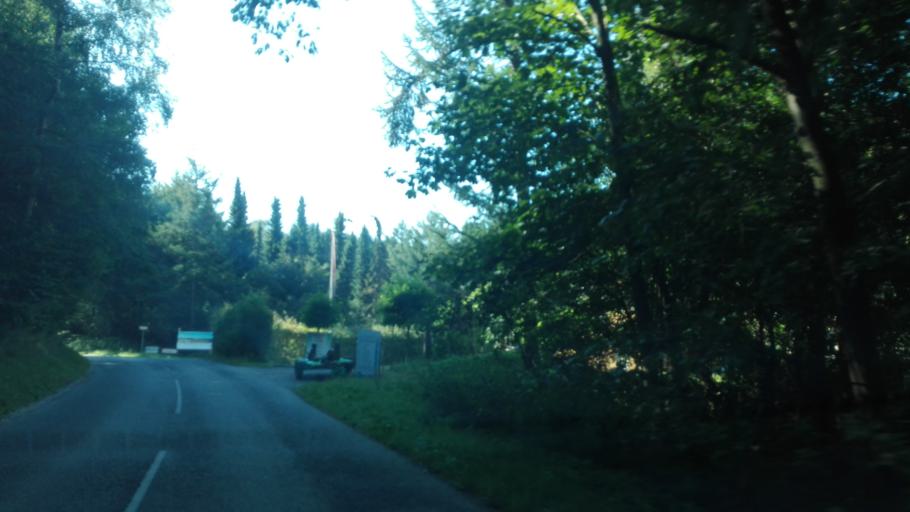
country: DK
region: Central Jutland
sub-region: Syddjurs Kommune
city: Ebeltoft
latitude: 56.2563
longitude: 10.6221
